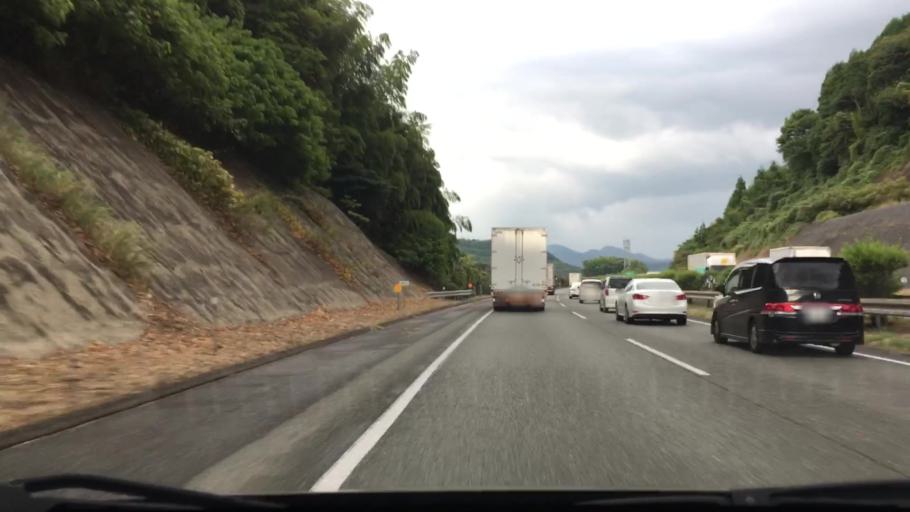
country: JP
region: Fukuoka
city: Miyata
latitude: 33.7508
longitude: 130.5794
